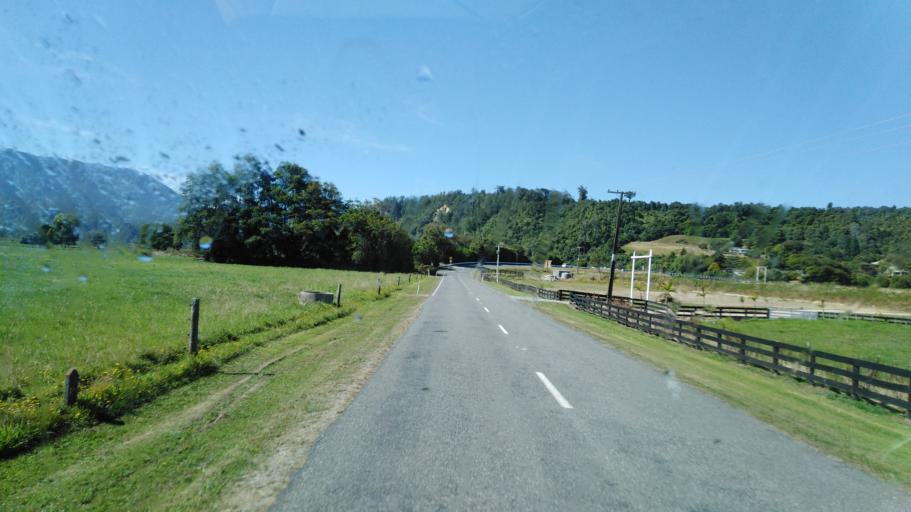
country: NZ
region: West Coast
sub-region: Buller District
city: Westport
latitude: -41.2578
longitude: 172.1316
